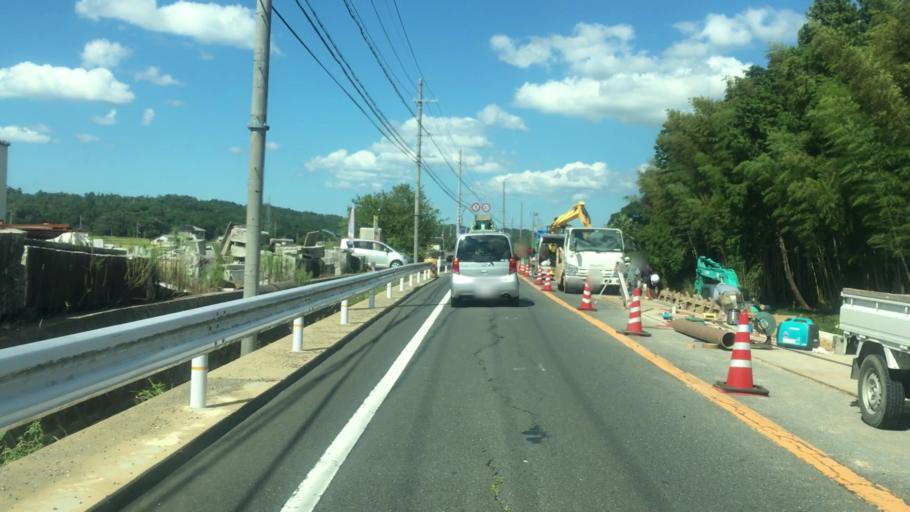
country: JP
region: Kyoto
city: Miyazu
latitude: 35.5959
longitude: 135.0439
